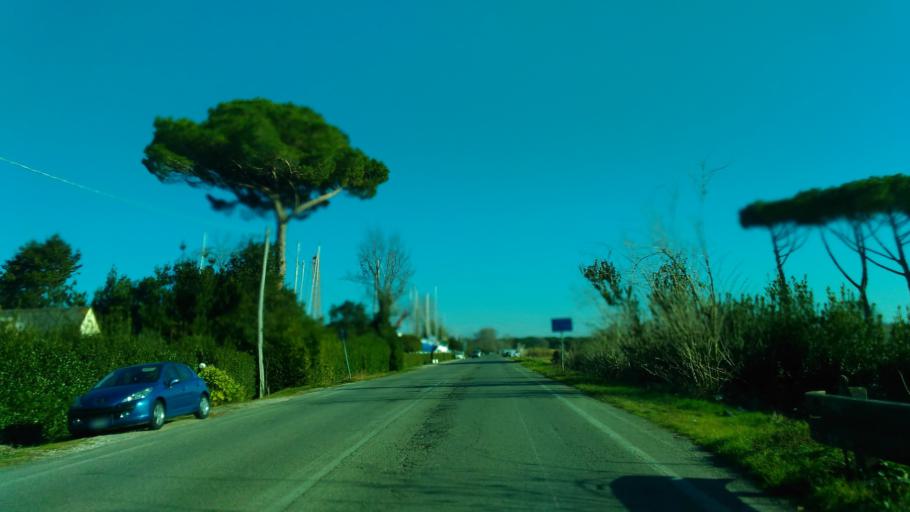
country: IT
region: Tuscany
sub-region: Province of Pisa
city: Marina di Pisa
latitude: 43.6764
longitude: 10.3111
